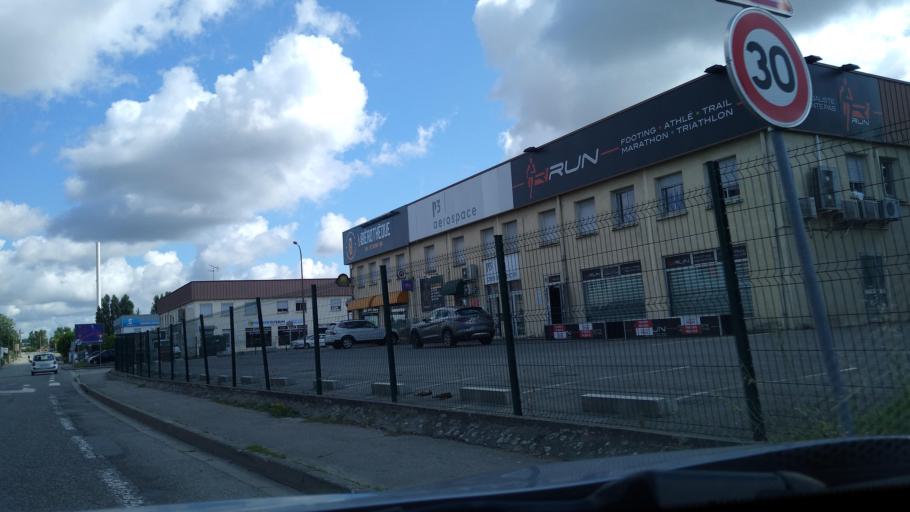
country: FR
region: Midi-Pyrenees
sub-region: Departement de la Haute-Garonne
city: L'Union
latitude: 43.6341
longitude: 1.4820
